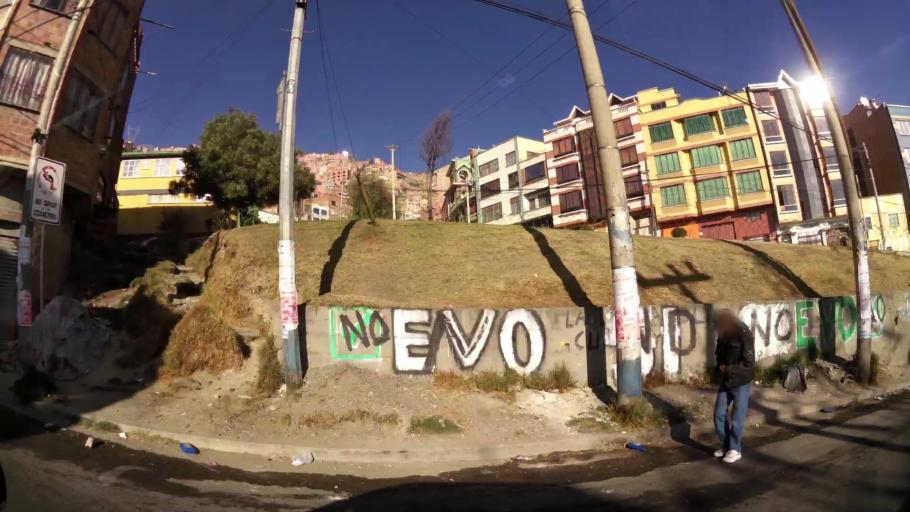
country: BO
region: La Paz
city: La Paz
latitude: -16.5013
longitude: -68.1540
